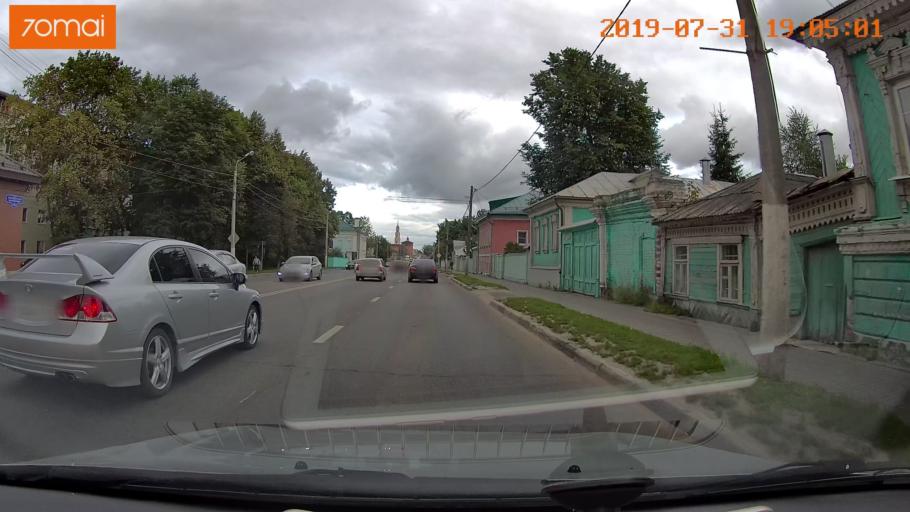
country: RU
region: Moskovskaya
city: Raduzhnyy
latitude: 55.1071
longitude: 38.7441
